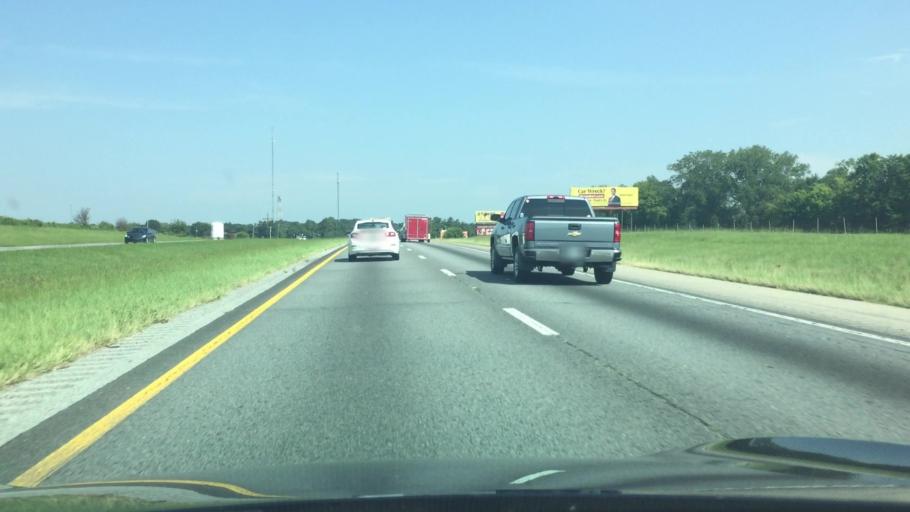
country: US
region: Alabama
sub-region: Autauga County
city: Pine Level
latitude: 32.6177
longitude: -86.4843
